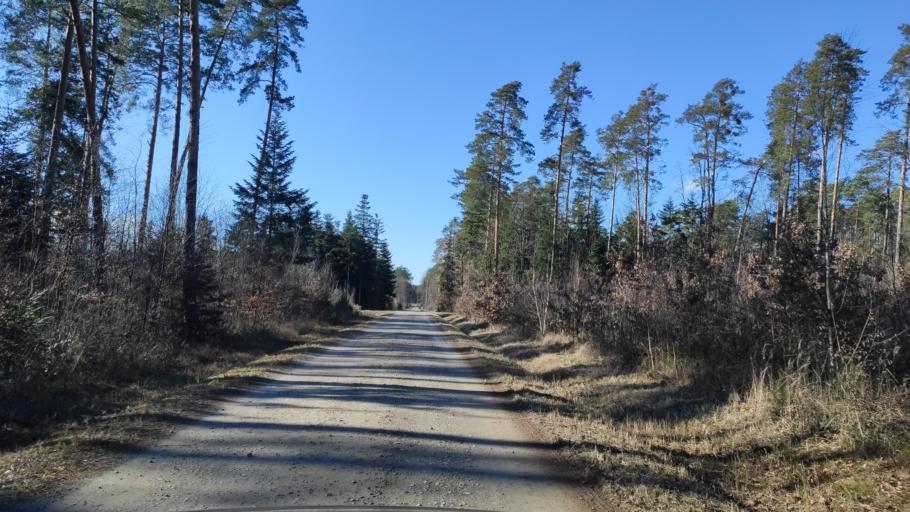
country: PL
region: Masovian Voivodeship
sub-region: Powiat radomski
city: Jedlnia-Letnisko
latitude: 51.4700
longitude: 21.3056
